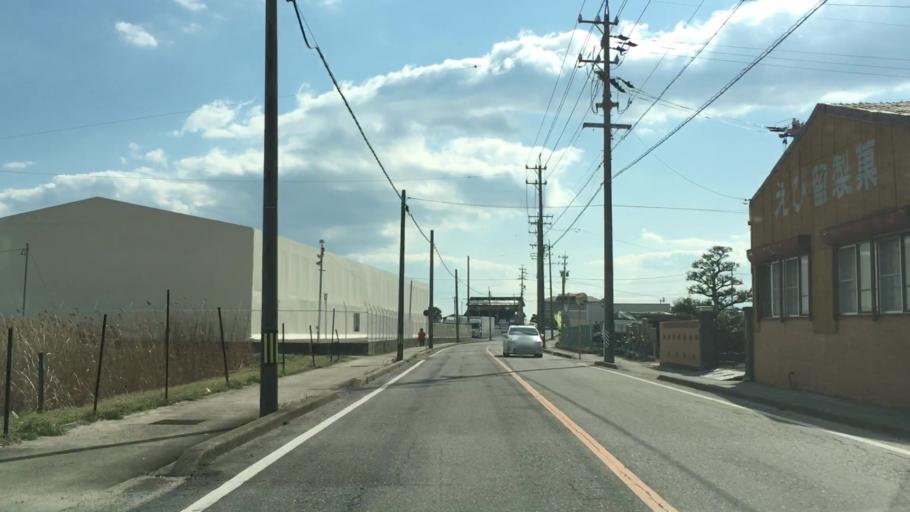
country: JP
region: Aichi
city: Ishiki
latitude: 34.7863
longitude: 137.0316
